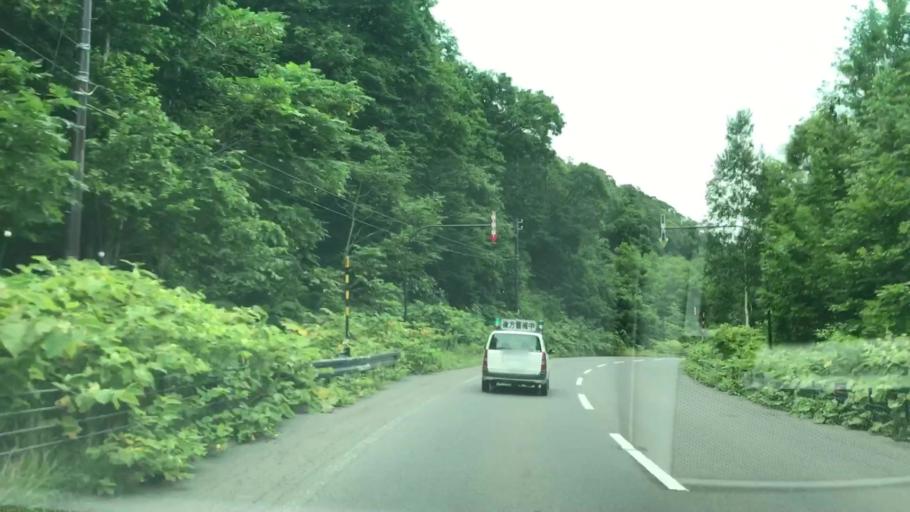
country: JP
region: Hokkaido
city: Yoichi
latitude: 43.0217
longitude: 140.8675
